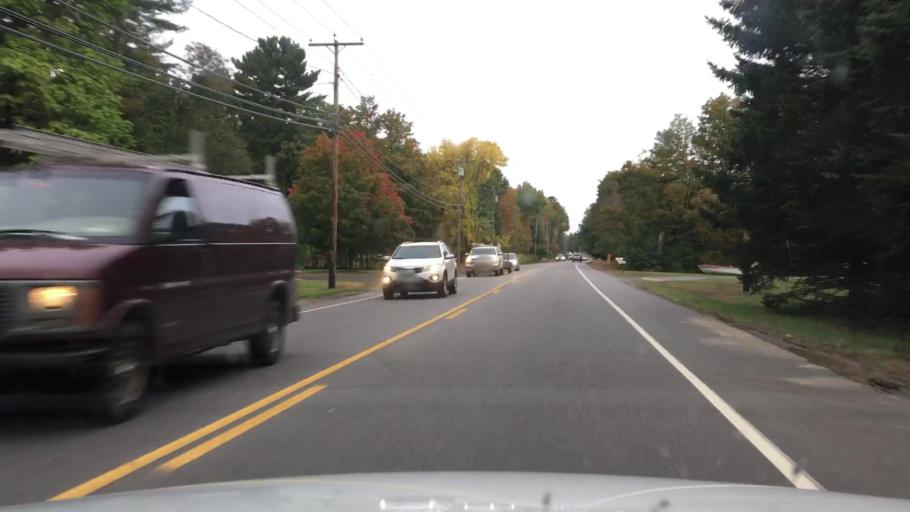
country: US
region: Maine
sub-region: Cumberland County
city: New Gloucester
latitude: 43.9093
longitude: -70.3504
